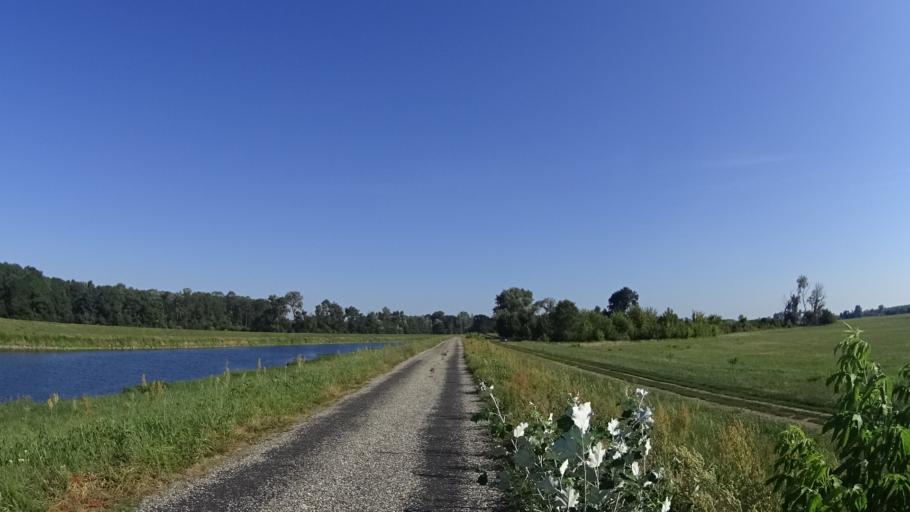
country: CZ
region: South Moravian
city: Tvrdonice
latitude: 48.7244
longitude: 17.0143
